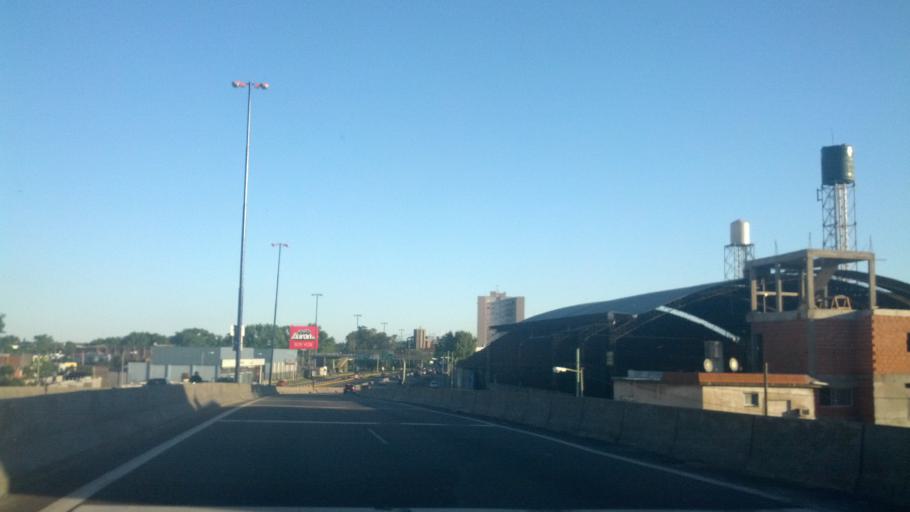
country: AR
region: Buenos Aires
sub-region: Partido de Lomas de Zamora
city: Lomas de Zamora
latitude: -34.7564
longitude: -58.4330
